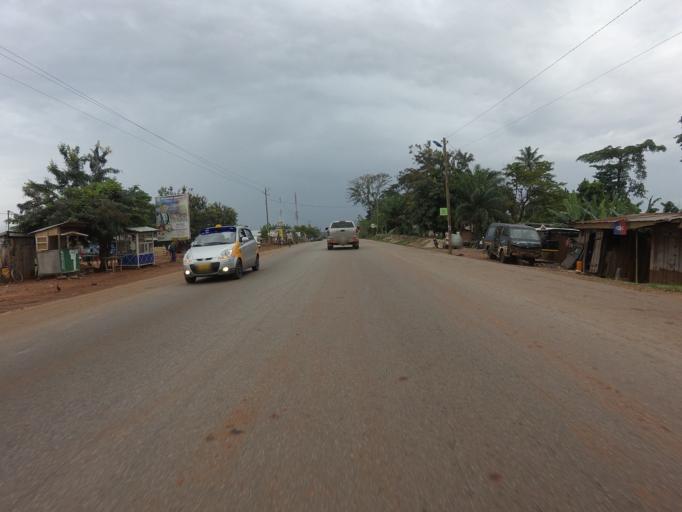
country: GH
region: Ashanti
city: Konongo
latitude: 6.6232
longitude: -1.2017
